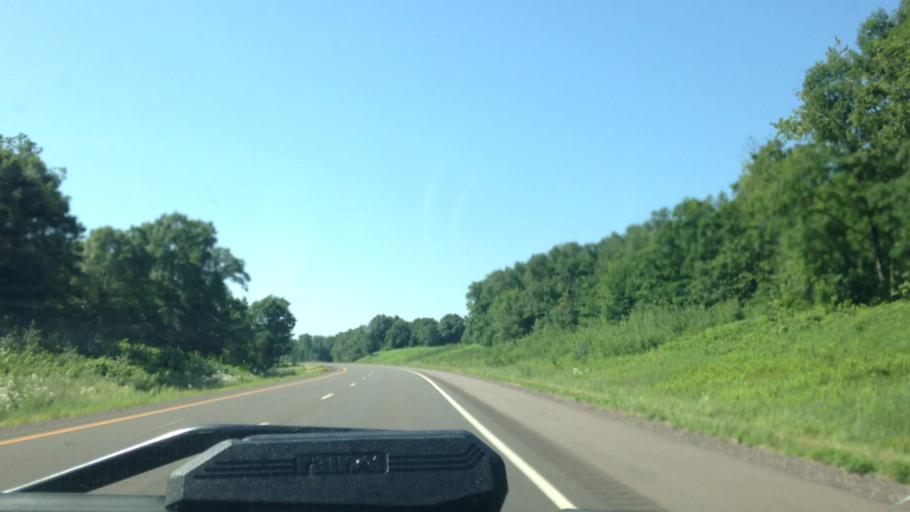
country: US
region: Wisconsin
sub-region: Washburn County
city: Spooner
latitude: 45.9476
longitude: -91.8290
